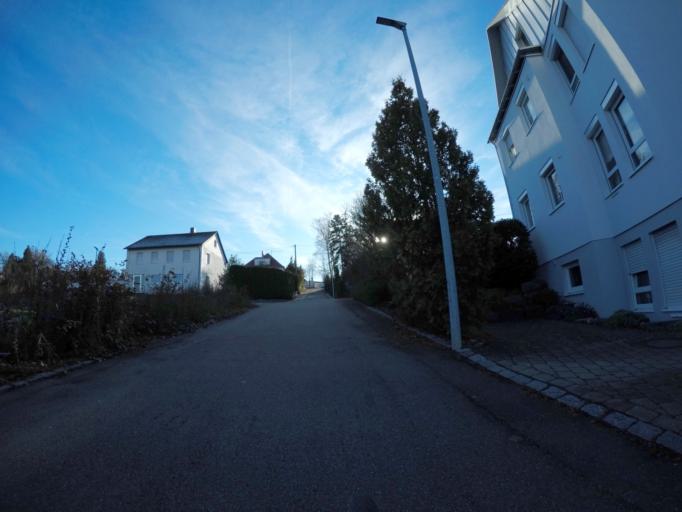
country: DE
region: Baden-Wuerttemberg
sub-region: Tuebingen Region
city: Eningen unter Achalm
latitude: 48.5164
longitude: 9.2372
